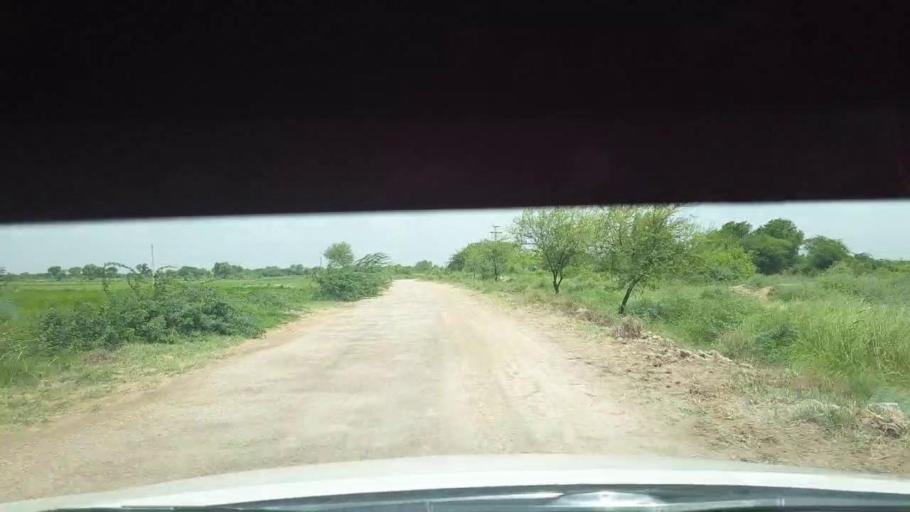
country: PK
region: Sindh
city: Kadhan
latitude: 24.5160
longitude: 68.9721
